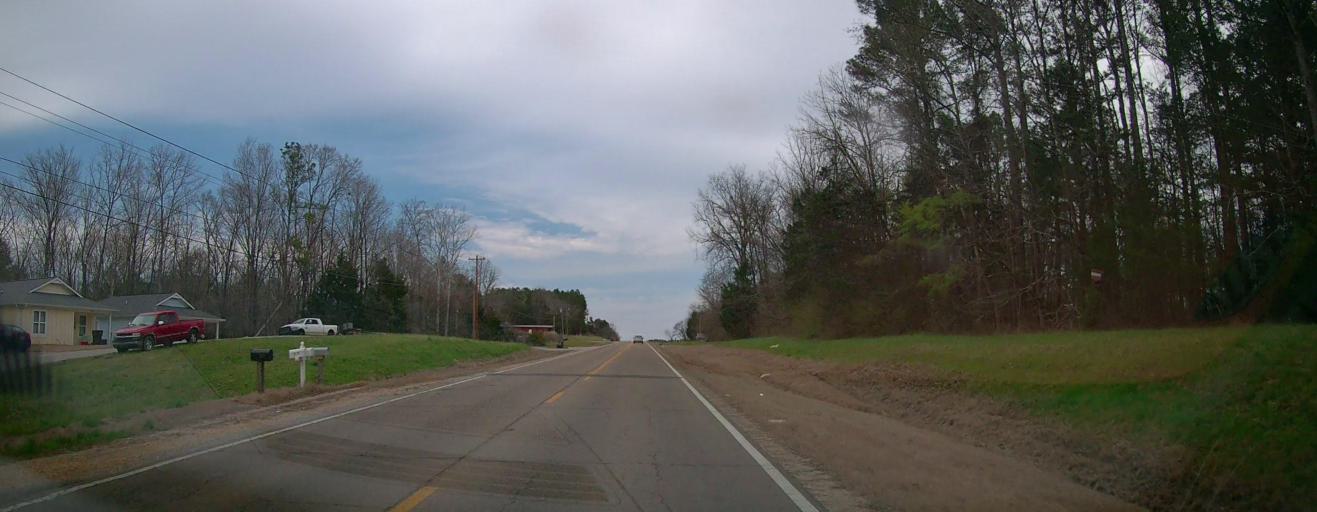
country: US
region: Mississippi
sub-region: Lee County
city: Plantersville
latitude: 34.2659
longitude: -88.6159
